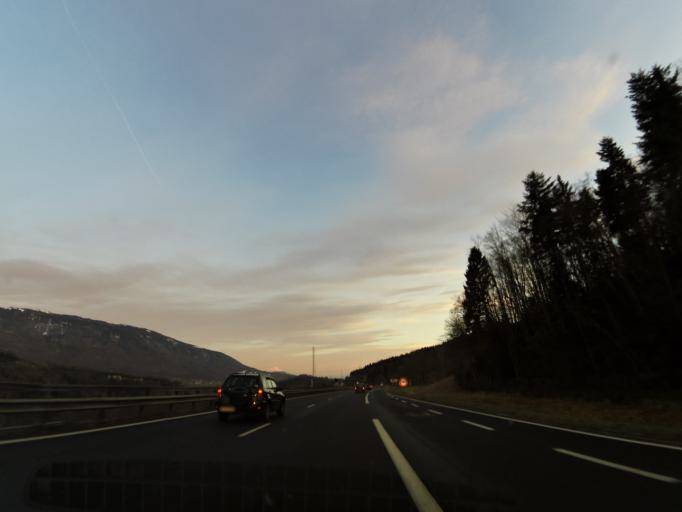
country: FR
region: Rhone-Alpes
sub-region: Departement de l'Ain
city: Chatillon-en-Michaille
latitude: 46.1589
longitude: 5.7811
